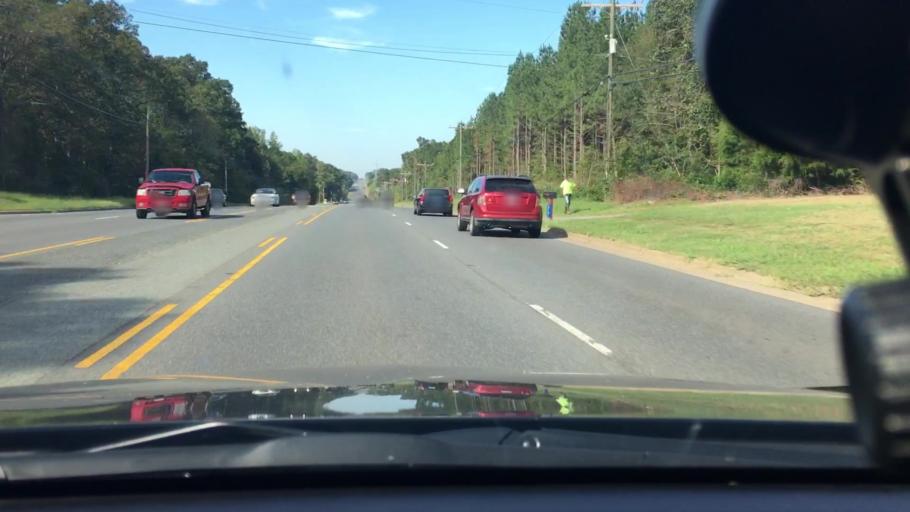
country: US
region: North Carolina
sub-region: Cabarrus County
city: Midland
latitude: 35.2500
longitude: -80.5119
